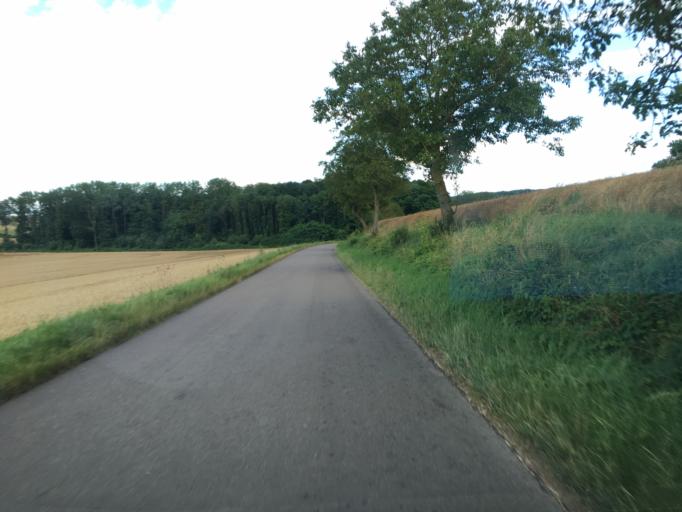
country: FR
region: Bourgogne
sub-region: Departement de l'Yonne
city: Appoigny
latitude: 47.8785
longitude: 3.4933
